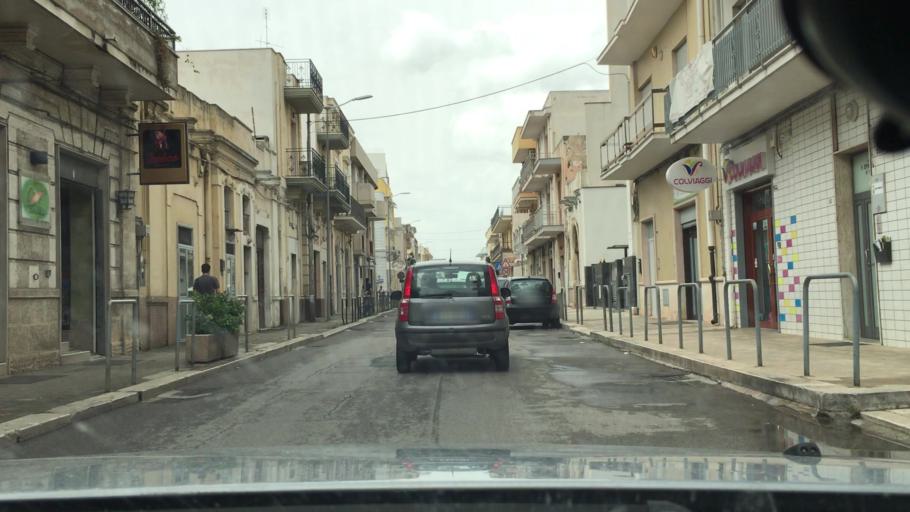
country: IT
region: Apulia
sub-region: Provincia di Bari
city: Capurso
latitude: 41.0484
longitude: 16.9242
